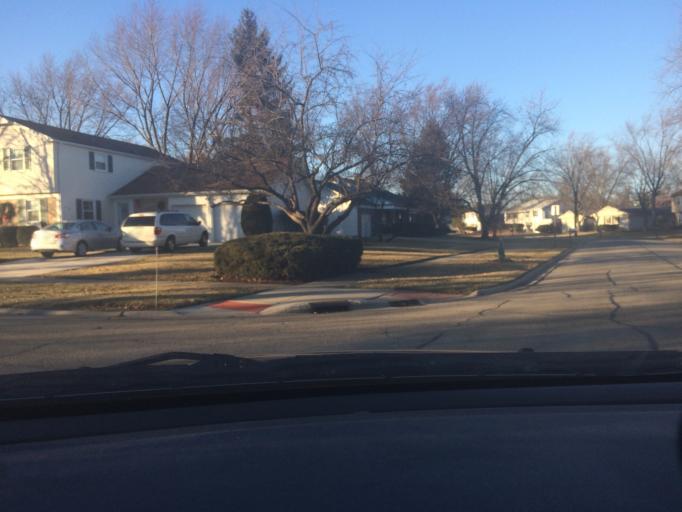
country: US
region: Illinois
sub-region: Cook County
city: Buffalo Grove
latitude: 42.1641
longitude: -87.9752
